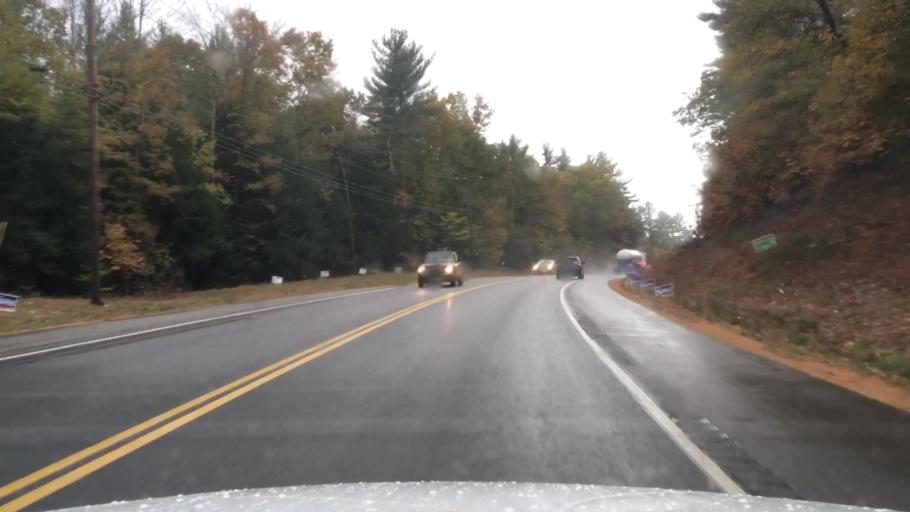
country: US
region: New Hampshire
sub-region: Strafford County
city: Barrington
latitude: 43.2285
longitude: -70.9915
